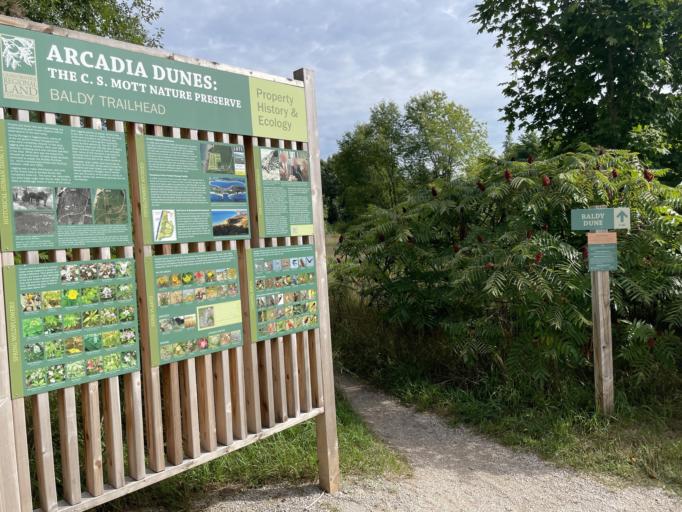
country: US
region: Michigan
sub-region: Benzie County
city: Frankfort
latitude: 44.5259
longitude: -86.2230
